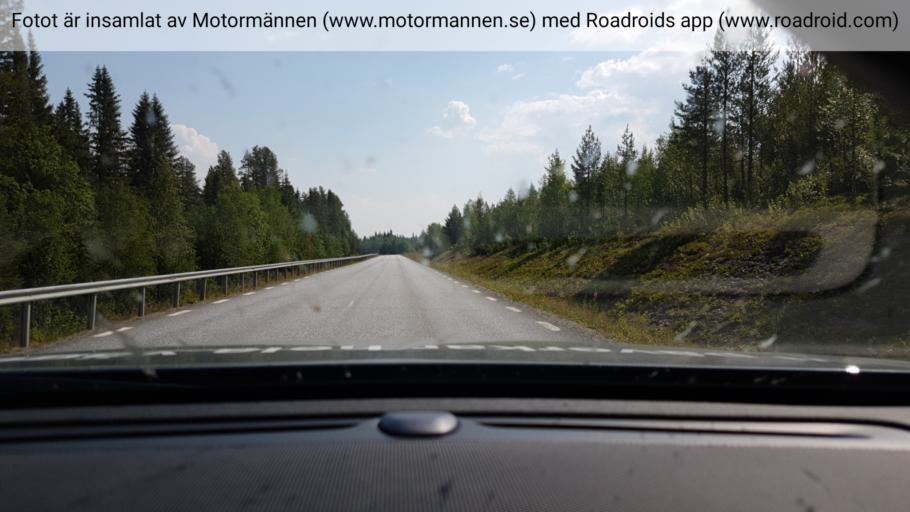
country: SE
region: Vaesterbotten
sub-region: Storumans Kommun
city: Fristad
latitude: 65.3989
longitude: 16.3839
